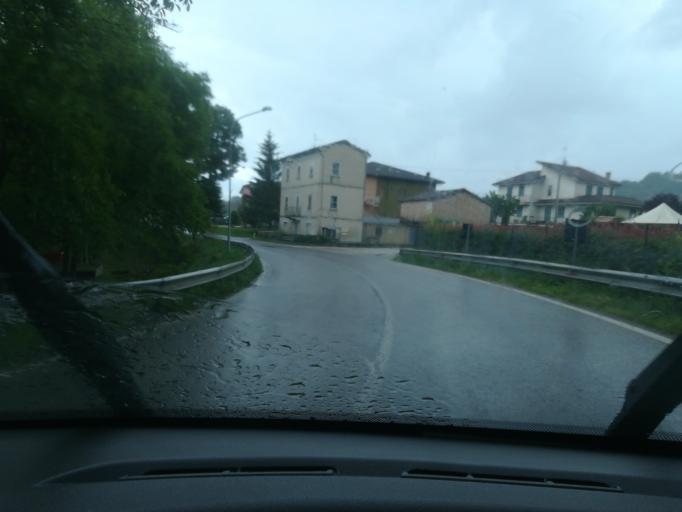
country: IT
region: The Marches
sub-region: Provincia di Macerata
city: Sarnano
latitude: 43.0309
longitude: 13.3026
